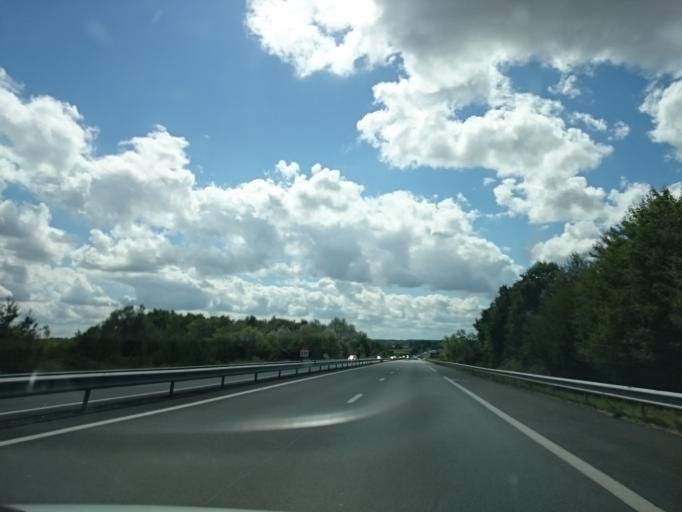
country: FR
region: Pays de la Loire
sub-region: Departement de Maine-et-Loire
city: Seiches-sur-le-Loir
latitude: 47.6035
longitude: -0.3060
